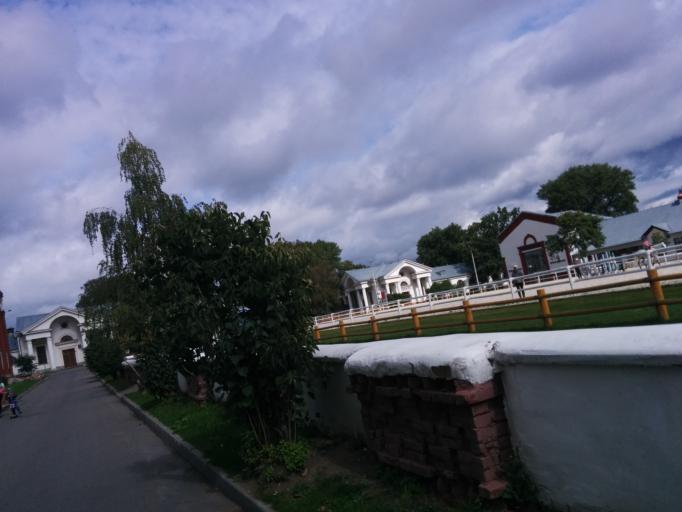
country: RU
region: Moscow
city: Ostankinskiy
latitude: 55.8370
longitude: 37.6227
